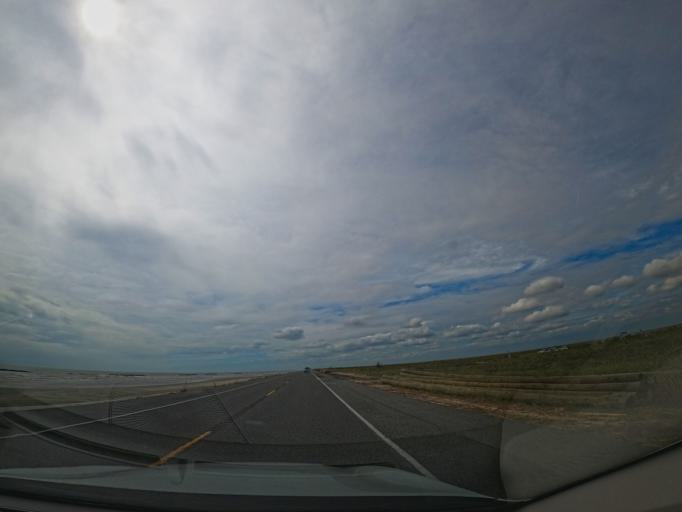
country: US
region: Louisiana
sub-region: Cameron Parish
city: Cameron
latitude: 29.7673
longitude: -93.5125
